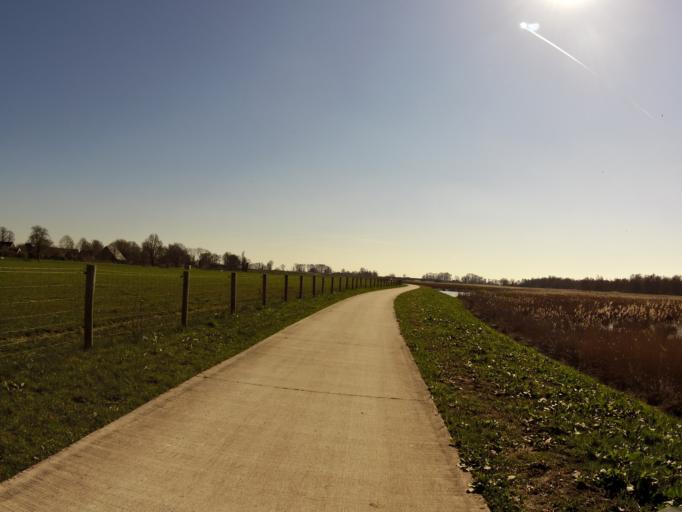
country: NL
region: Overijssel
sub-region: Gemeente Steenwijkerland
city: Blokzijl
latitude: 52.7509
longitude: 5.9917
